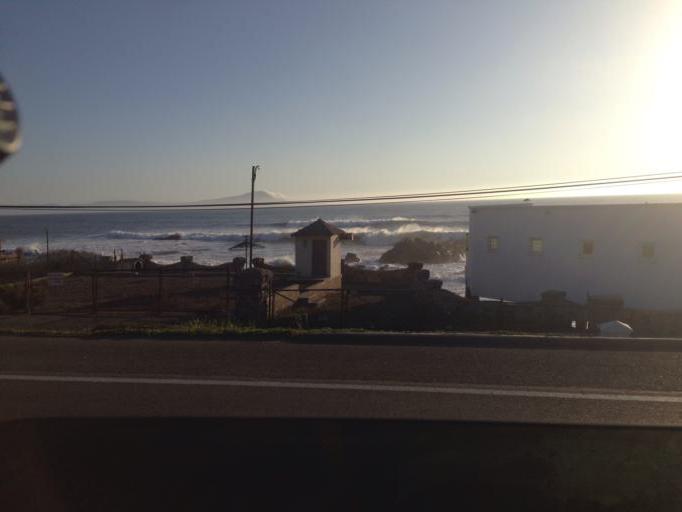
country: MX
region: Baja California
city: El Sauzal
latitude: 31.8684
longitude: -116.6738
